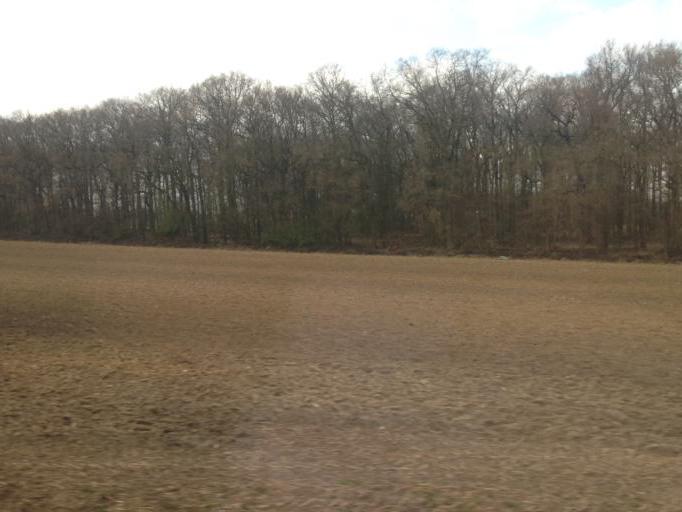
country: DE
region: North Rhine-Westphalia
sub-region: Regierungsbezirk Munster
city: Nottuln
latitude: 51.8712
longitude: 7.3893
